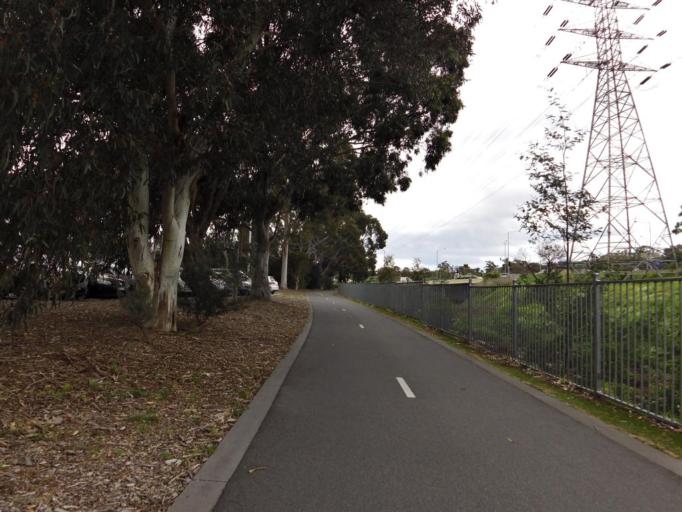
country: AU
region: Victoria
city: Glenferrie
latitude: -37.8434
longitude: 145.0405
